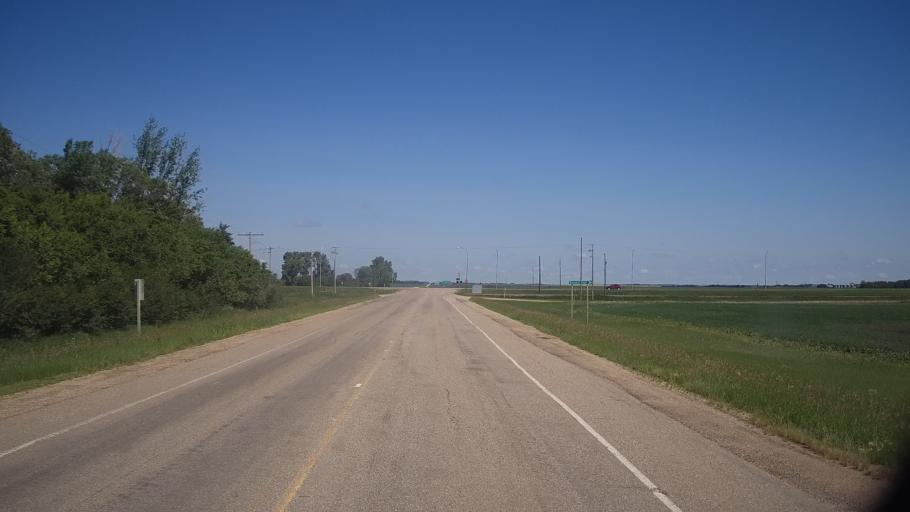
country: CA
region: Saskatchewan
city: Saskatoon
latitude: 51.9892
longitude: -106.0754
